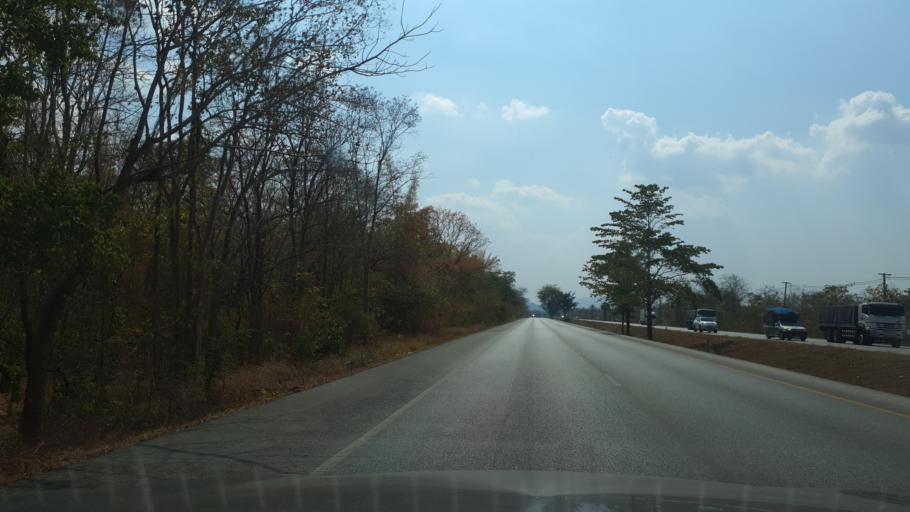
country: TH
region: Lampang
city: Mae Phrik
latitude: 17.4347
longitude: 99.1586
